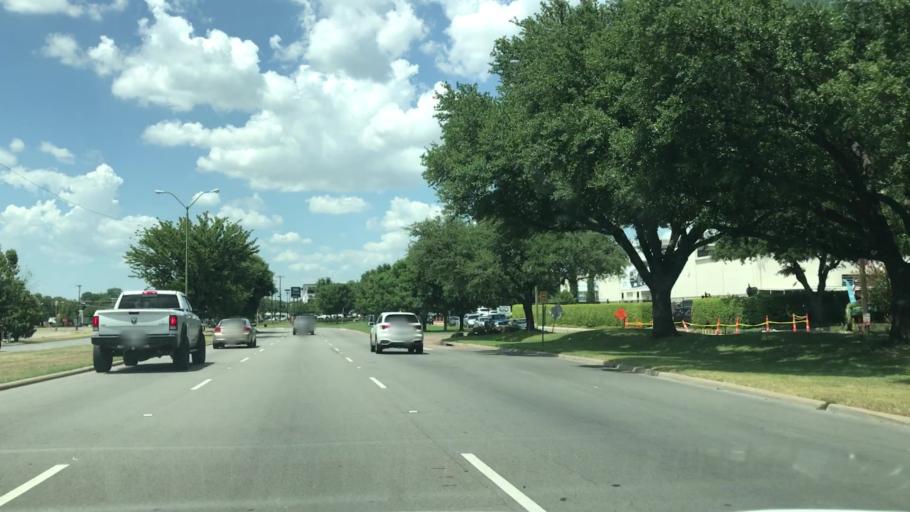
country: US
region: Texas
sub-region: Dallas County
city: University Park
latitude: 32.8428
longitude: -96.8345
